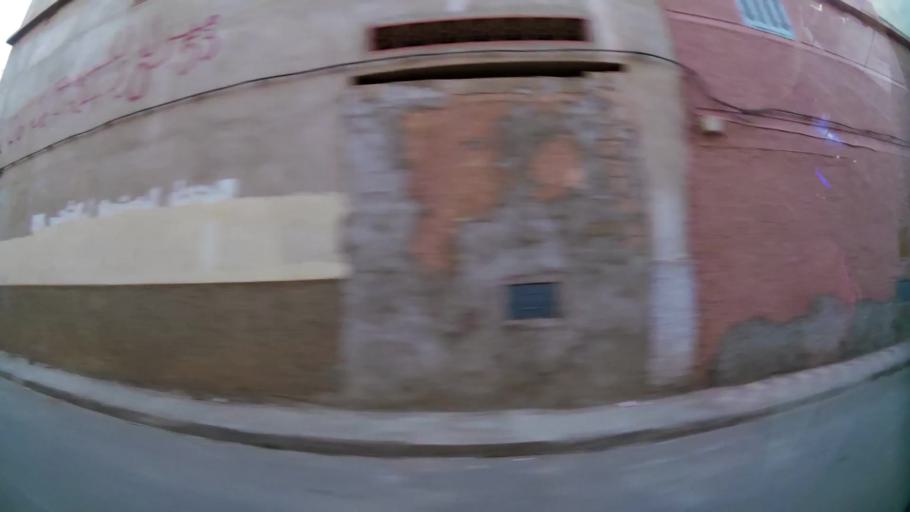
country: MA
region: Oriental
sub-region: Berkane-Taourirt
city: Berkane
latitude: 34.9193
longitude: -2.3194
